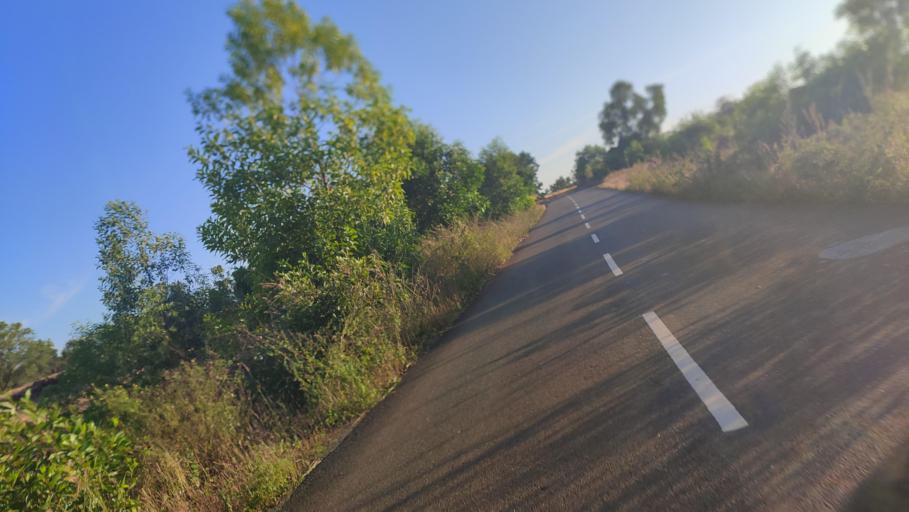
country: IN
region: Kerala
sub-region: Kasaragod District
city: Kasaragod
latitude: 12.4456
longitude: 75.0992
